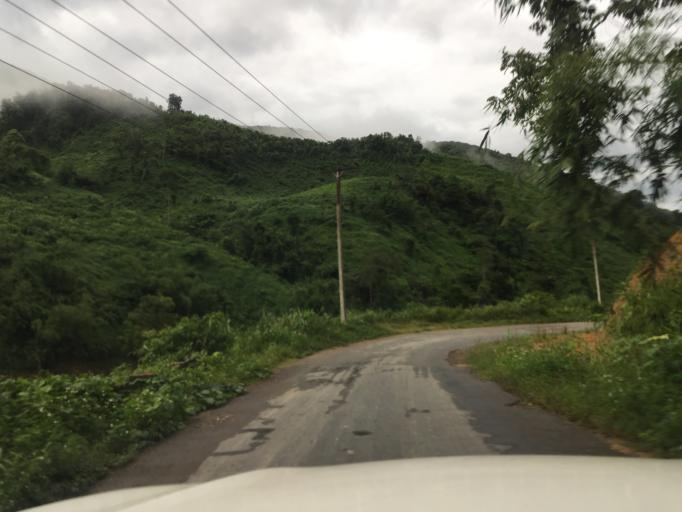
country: LA
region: Oudomxai
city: Muang La
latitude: 21.0299
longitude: 102.2367
